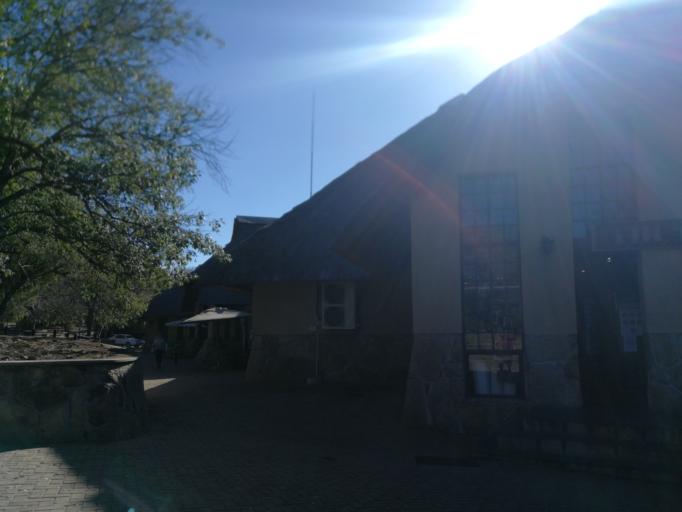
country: ZA
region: Limpopo
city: Thulamahashi
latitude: -24.9930
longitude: 31.5926
